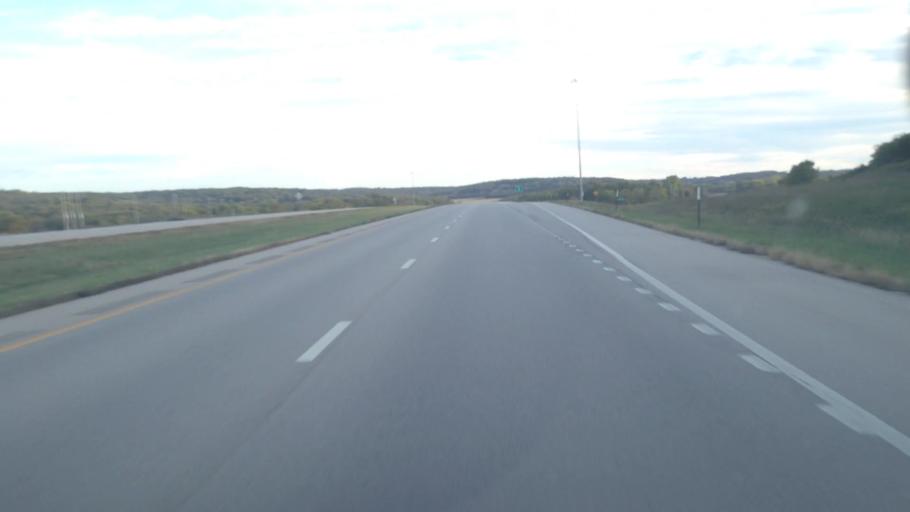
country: US
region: Kansas
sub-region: Douglas County
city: Lawrence
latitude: 38.8888
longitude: -95.2597
